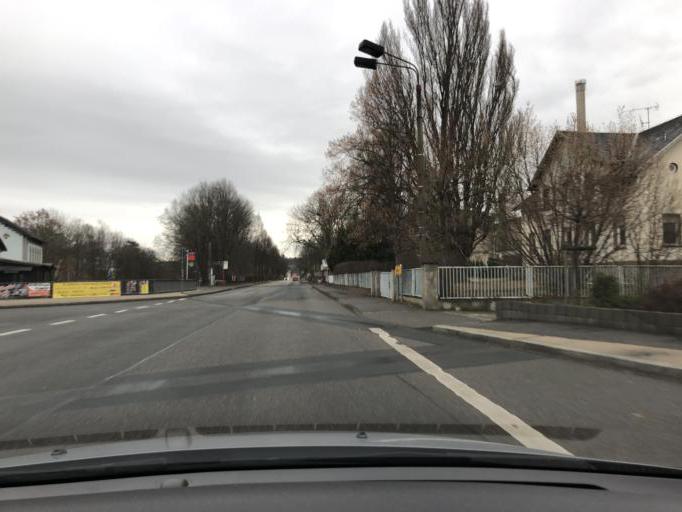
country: DE
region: Saxony
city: Dobeln
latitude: 51.1166
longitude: 13.1236
